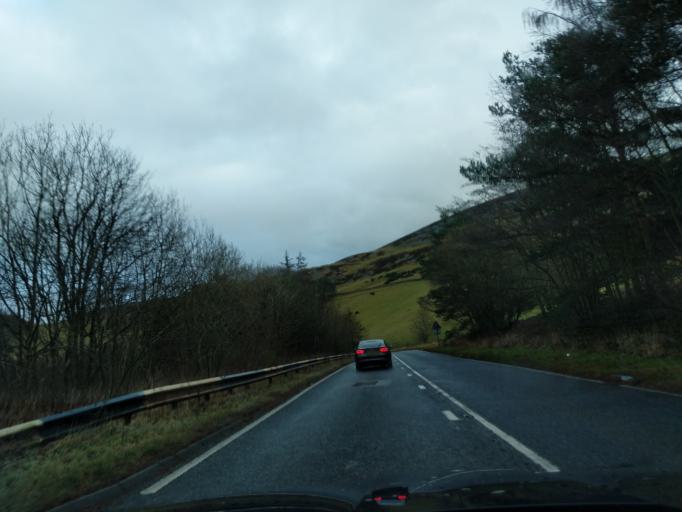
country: GB
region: Scotland
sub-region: The Scottish Borders
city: Galashiels
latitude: 55.6587
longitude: -2.8658
